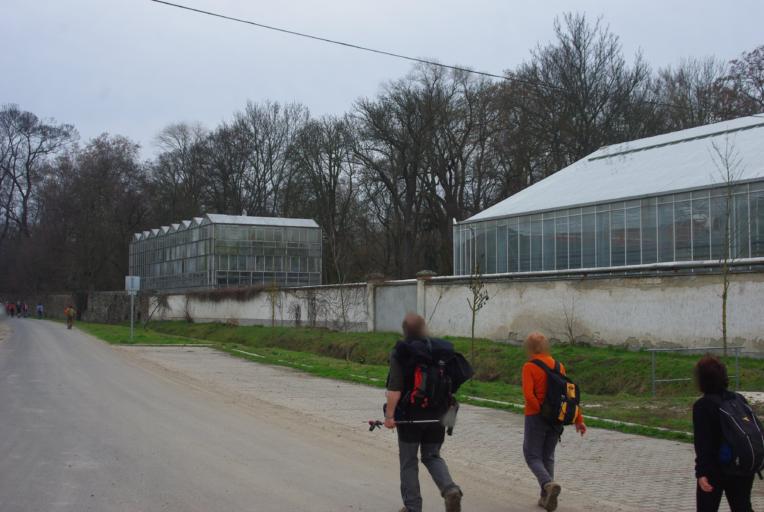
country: HU
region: Pest
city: Orbottyan
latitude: 47.7108
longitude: 19.2308
